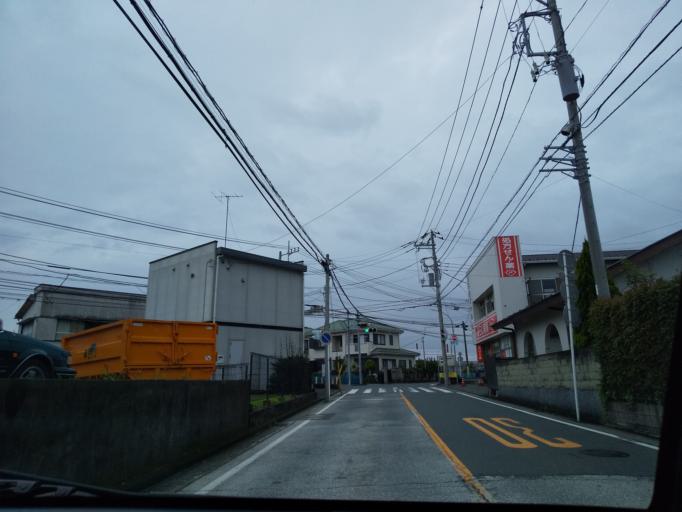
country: JP
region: Kanagawa
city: Fujisawa
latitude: 35.3925
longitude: 139.5061
